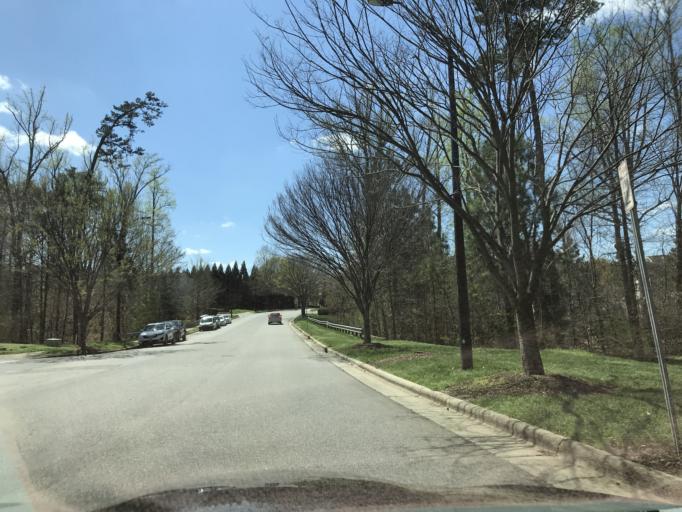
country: US
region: North Carolina
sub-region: Wake County
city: West Raleigh
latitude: 35.8628
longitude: -78.7185
